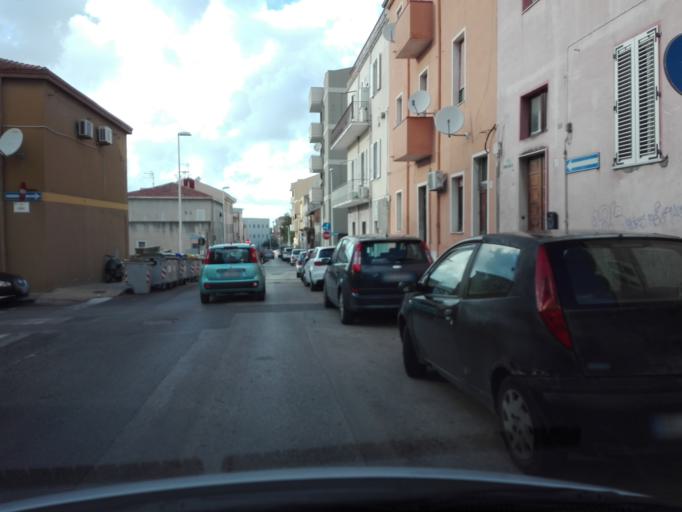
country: IT
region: Sardinia
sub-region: Provincia di Sassari
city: Sassari
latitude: 40.7342
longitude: 8.5653
